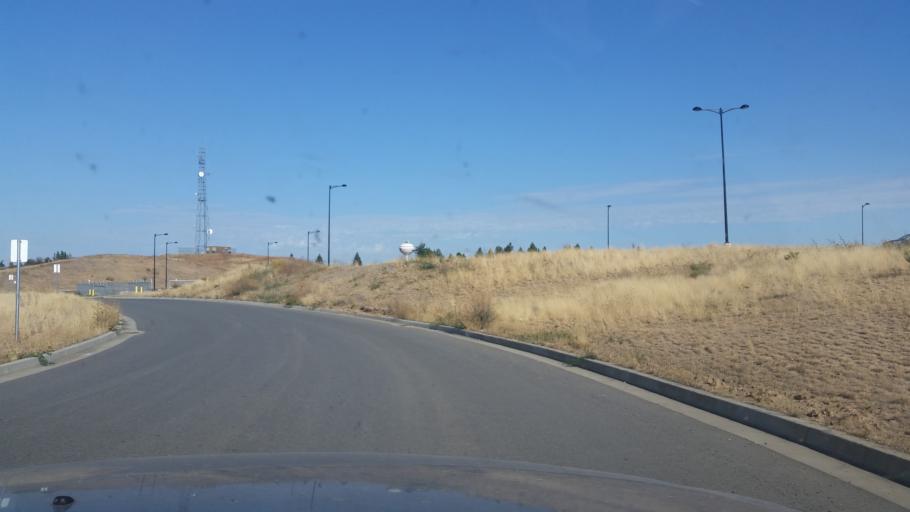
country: US
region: Washington
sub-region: Spokane County
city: Cheney
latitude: 47.4950
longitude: -117.5915
